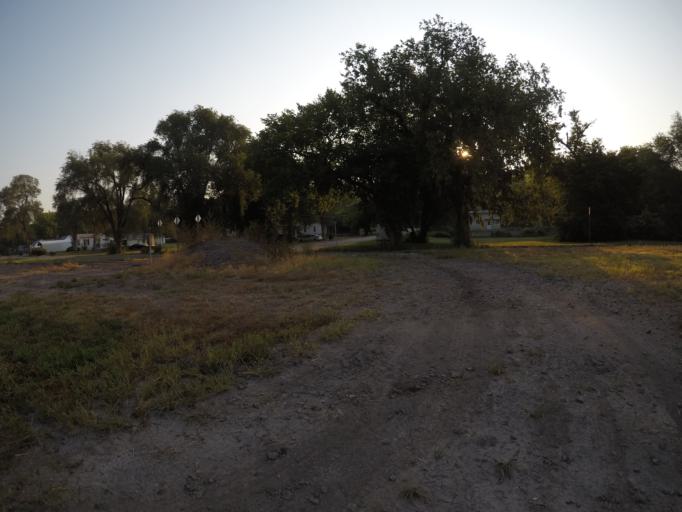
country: US
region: Kansas
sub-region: Marshall County
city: Marysville
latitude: 39.8460
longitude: -96.6495
